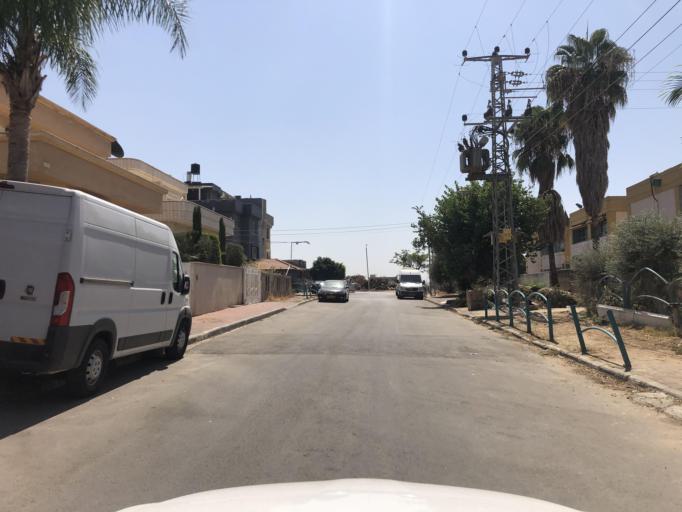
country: IL
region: Central District
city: Jaljulya
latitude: 32.1562
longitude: 34.9570
